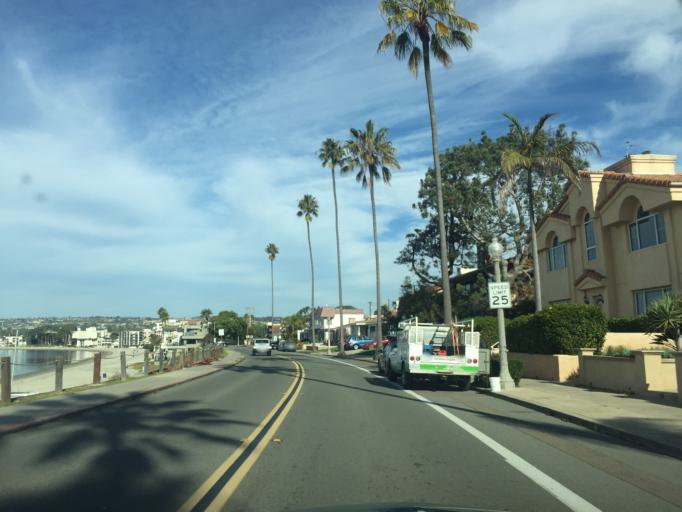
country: US
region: California
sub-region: San Diego County
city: La Jolla
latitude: 32.7847
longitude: -117.2395
